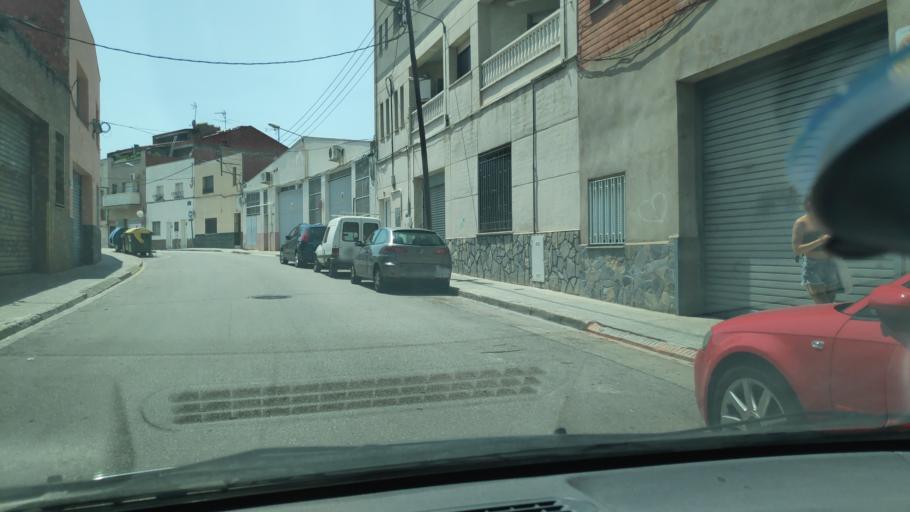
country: ES
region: Catalonia
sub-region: Provincia de Barcelona
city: Terrassa
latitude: 41.5616
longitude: 2.0385
